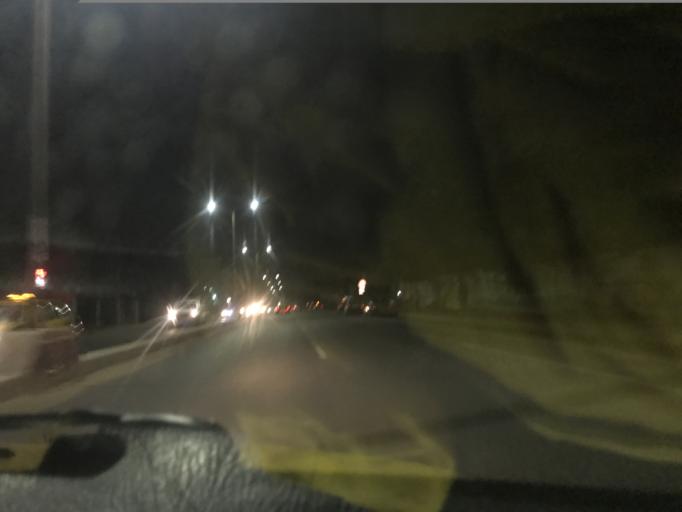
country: SN
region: Dakar
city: Mermoz Boabab
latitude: 14.6955
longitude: -17.4649
